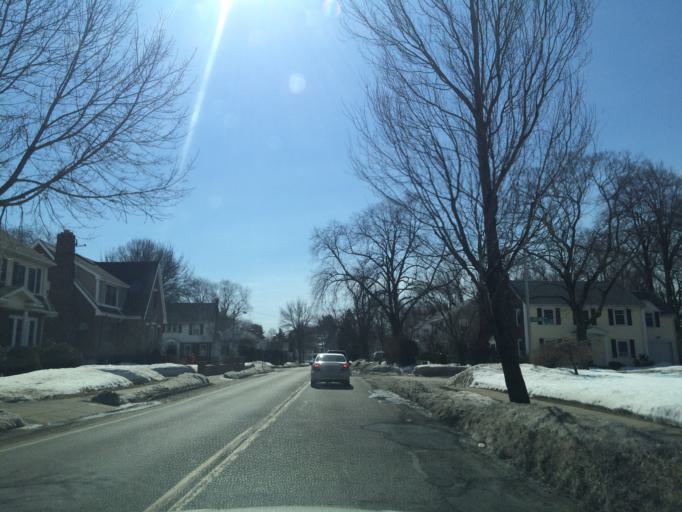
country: US
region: Massachusetts
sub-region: Middlesex County
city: Belmont
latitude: 42.4006
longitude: -71.1632
